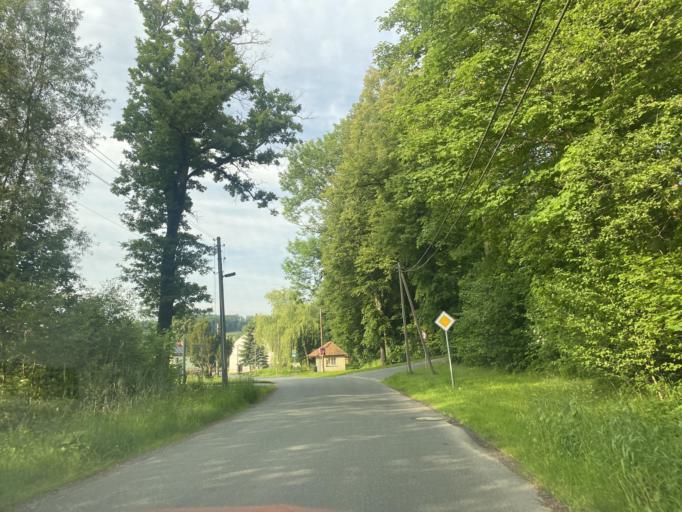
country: DE
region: Saxony
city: Bernstadt
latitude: 51.0263
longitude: 14.7993
